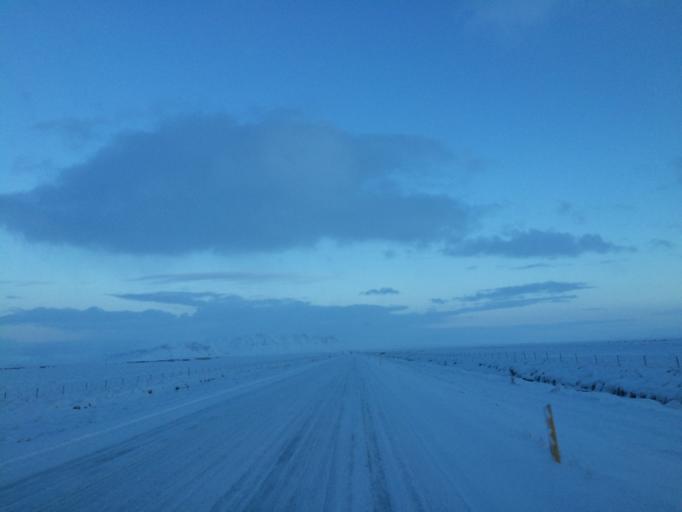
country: IS
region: South
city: Selfoss
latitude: 63.8726
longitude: -21.0964
